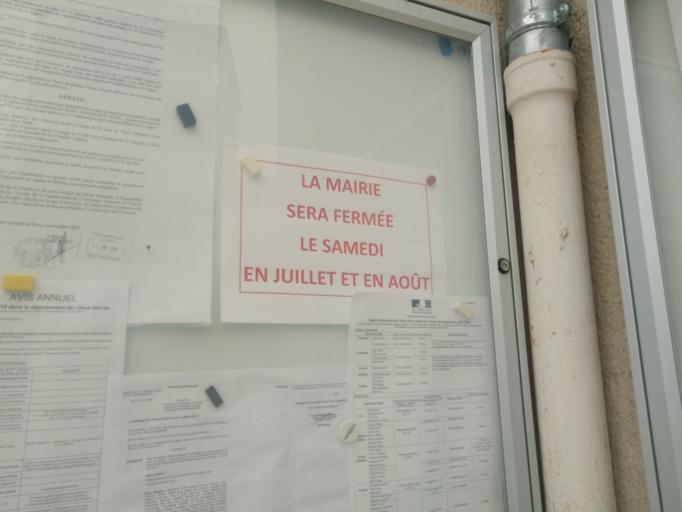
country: FR
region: Poitou-Charentes
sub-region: Departement des Deux-Sevres
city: Saint-Amand-sur-Sevre
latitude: 46.8687
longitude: -0.7949
